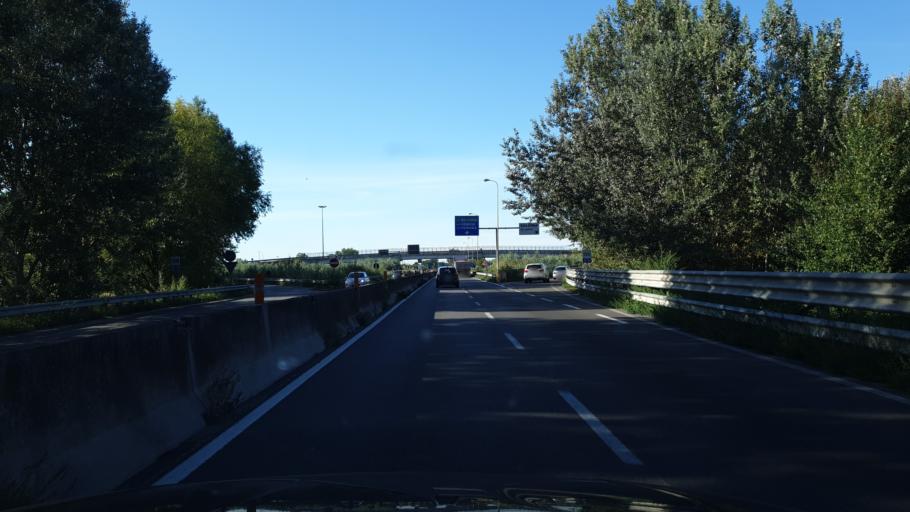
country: IT
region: Emilia-Romagna
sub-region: Provincia di Ravenna
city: Ravenna
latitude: 44.4087
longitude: 12.1741
